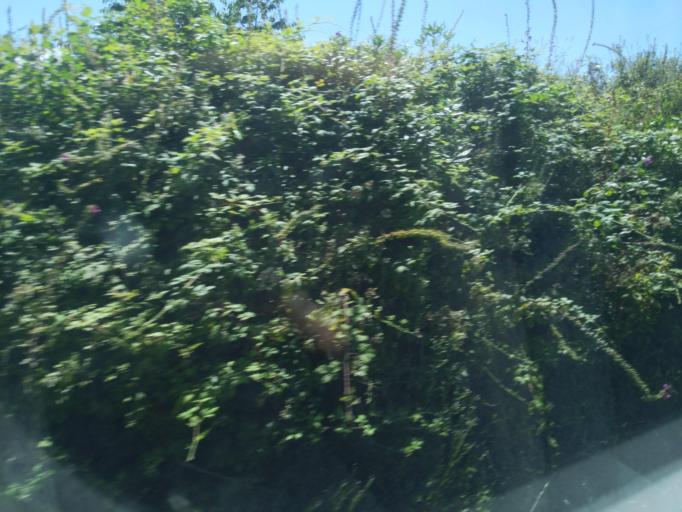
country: GB
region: England
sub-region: Cornwall
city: St Austell
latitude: 50.3433
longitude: -4.8101
